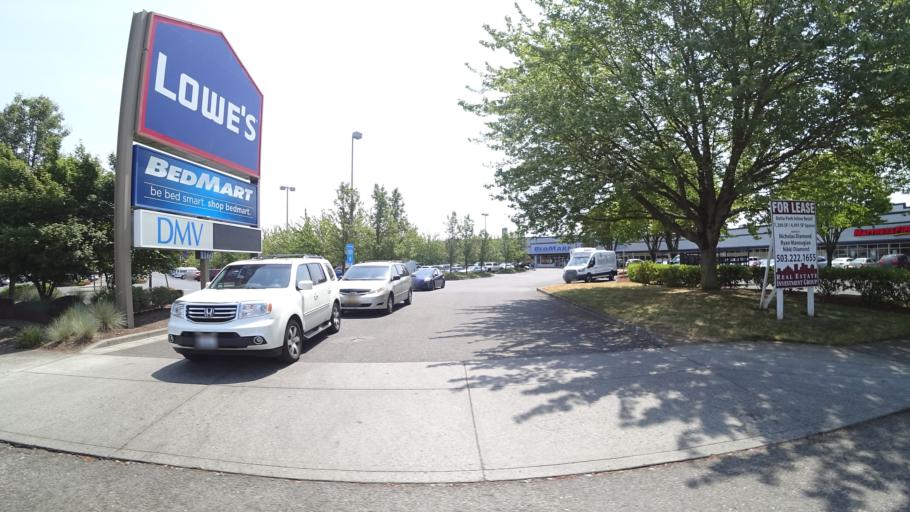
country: US
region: Washington
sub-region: Clark County
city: Vancouver
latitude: 45.5930
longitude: -122.6790
